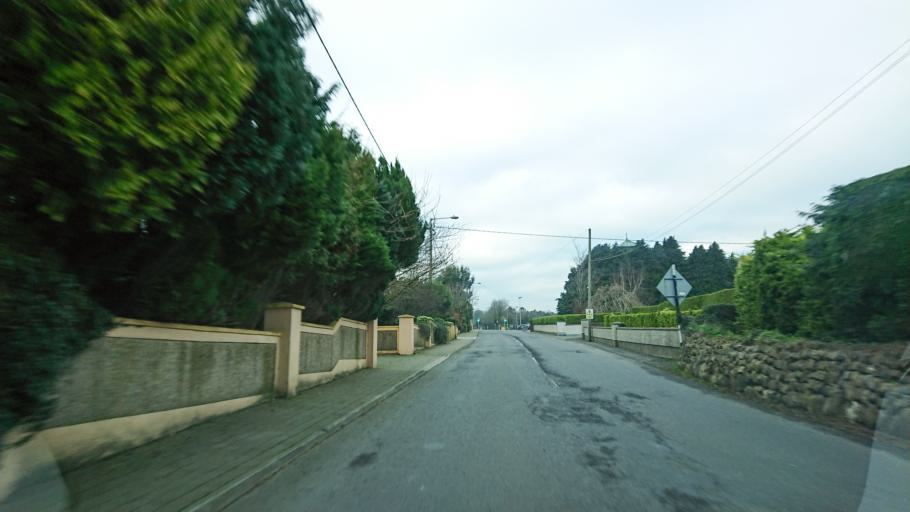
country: IE
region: Munster
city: Carrick-on-Suir
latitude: 52.3057
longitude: -7.4974
